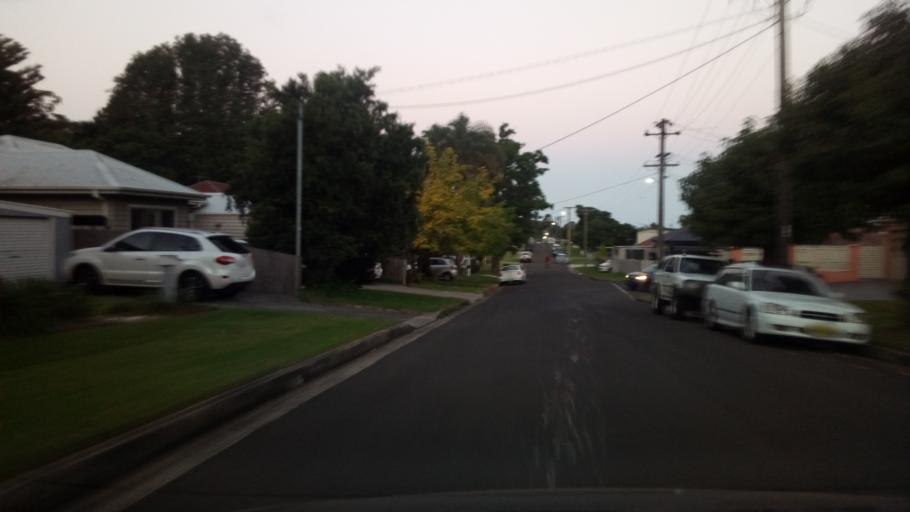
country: AU
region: New South Wales
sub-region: Wollongong
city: Mount Ousley
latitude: -34.3828
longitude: 150.8727
